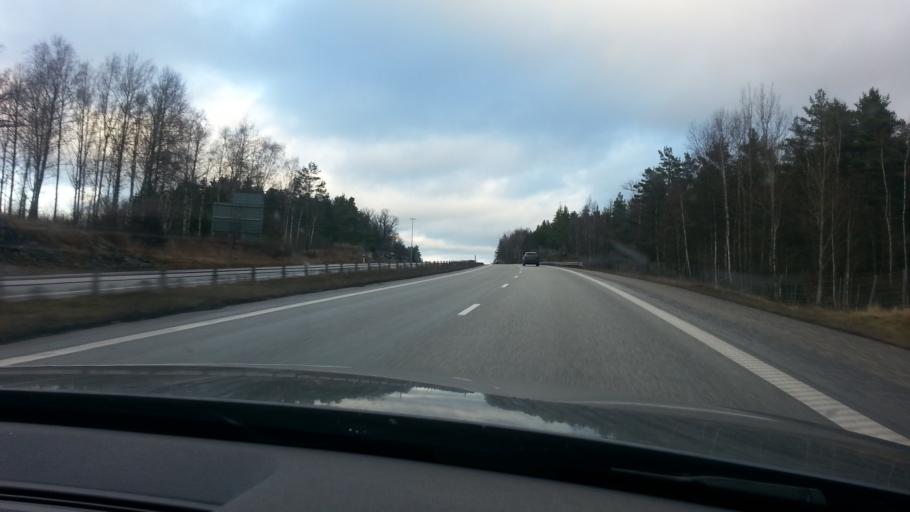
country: SE
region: Joenkoeping
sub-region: Jonkopings Kommun
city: Kaxholmen
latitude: 57.9357
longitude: 14.3325
